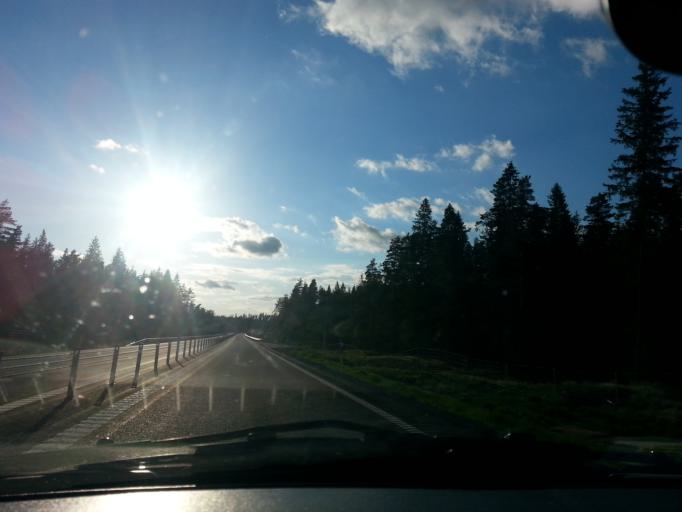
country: SE
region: Joenkoeping
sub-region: Gislaveds Kommun
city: Gislaved
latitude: 57.3192
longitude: 13.5564
